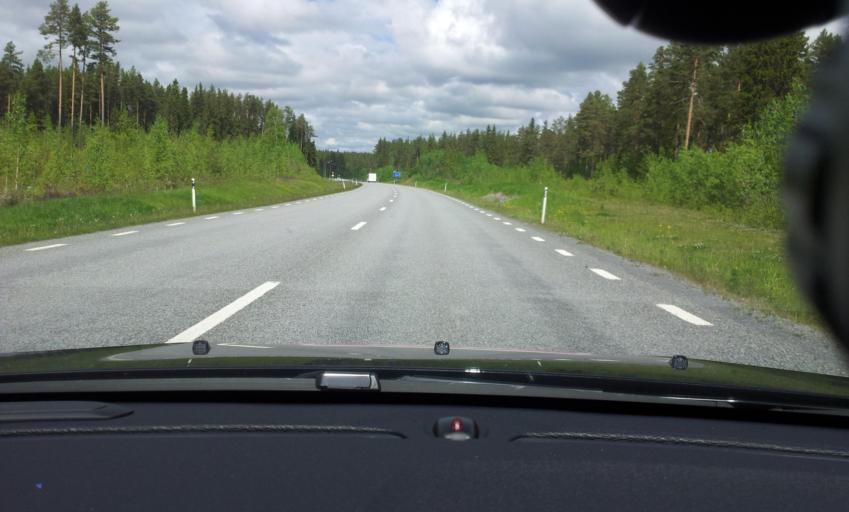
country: SE
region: Jaemtland
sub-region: OEstersunds Kommun
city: Lit
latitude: 63.3545
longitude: 14.8552
